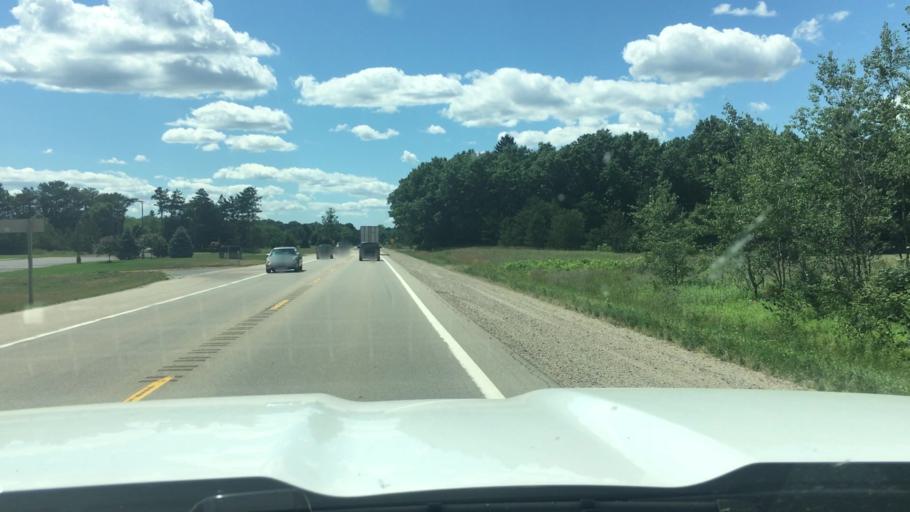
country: US
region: Michigan
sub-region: Kent County
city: Cedar Springs
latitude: 43.1758
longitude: -85.4831
